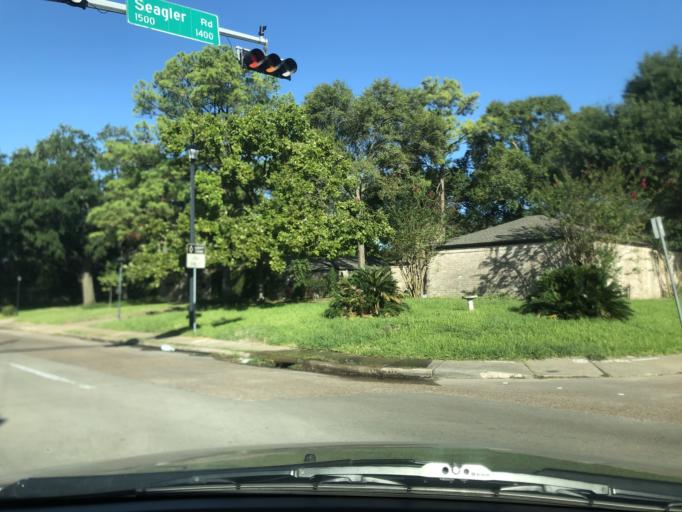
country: US
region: Texas
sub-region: Harris County
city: Bunker Hill Village
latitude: 29.7474
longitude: -95.5533
